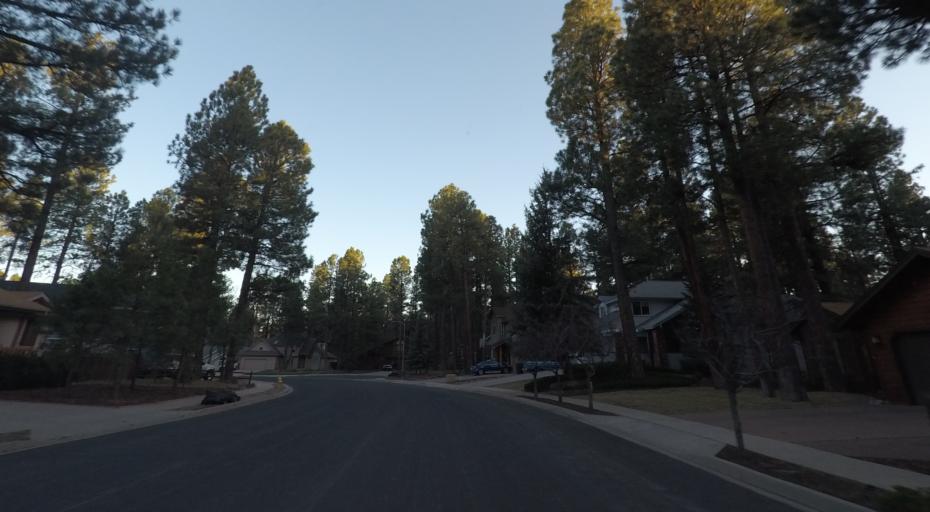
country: US
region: Arizona
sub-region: Coconino County
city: Flagstaff
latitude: 35.1745
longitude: -111.6833
